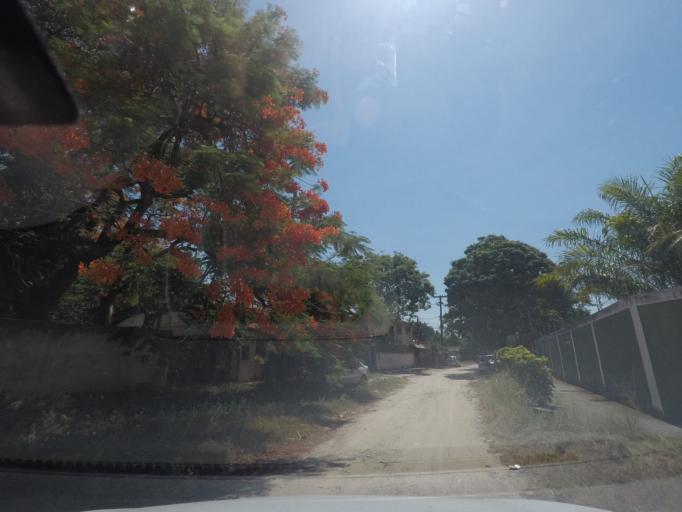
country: BR
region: Rio de Janeiro
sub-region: Niteroi
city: Niteroi
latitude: -22.9378
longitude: -43.0200
